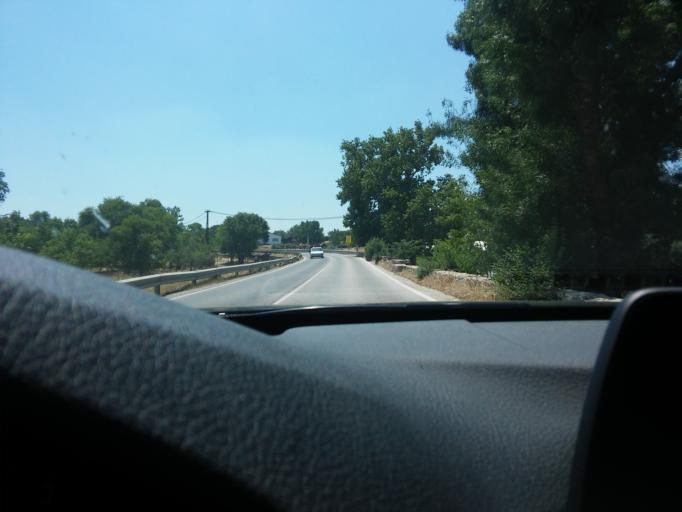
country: ES
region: Madrid
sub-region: Provincia de Madrid
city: Collado-Villalba
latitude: 40.6294
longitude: -4.0297
